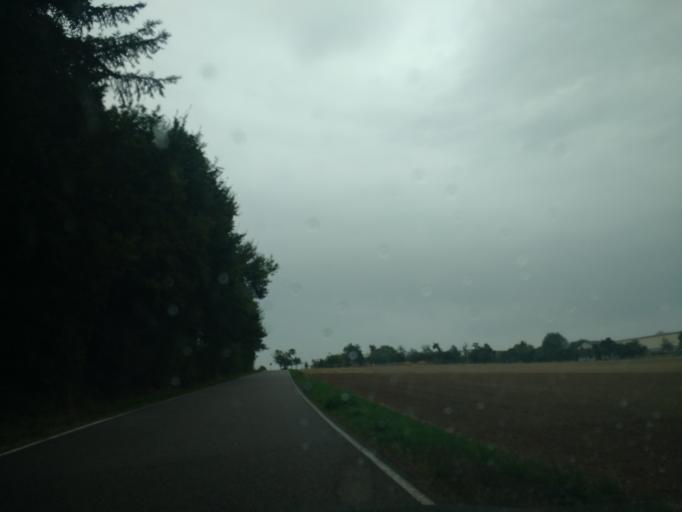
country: DE
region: Saarland
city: Perl
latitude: 49.4991
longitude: 6.4013
